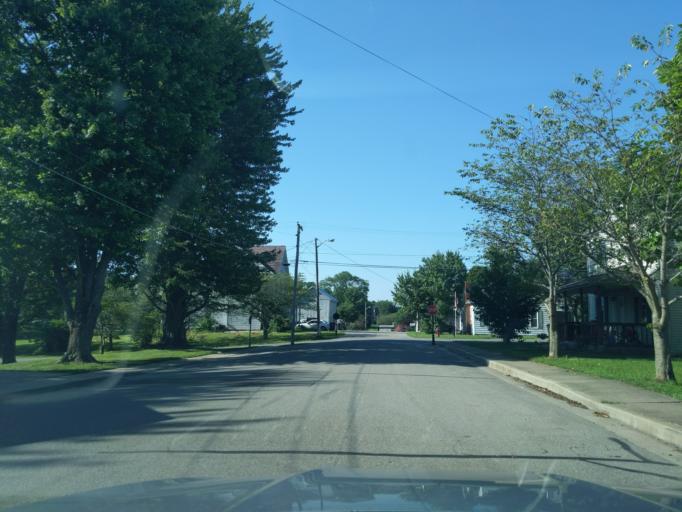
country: US
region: Indiana
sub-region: Ripley County
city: Versailles
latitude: 39.0721
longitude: -85.2535
